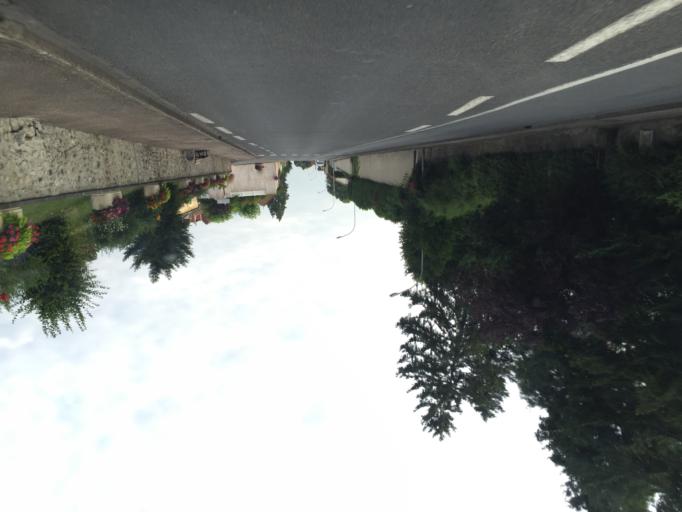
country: FR
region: Auvergne
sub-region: Departement de l'Allier
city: Saint-Germain-des-Fosses
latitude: 46.2083
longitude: 3.4328
